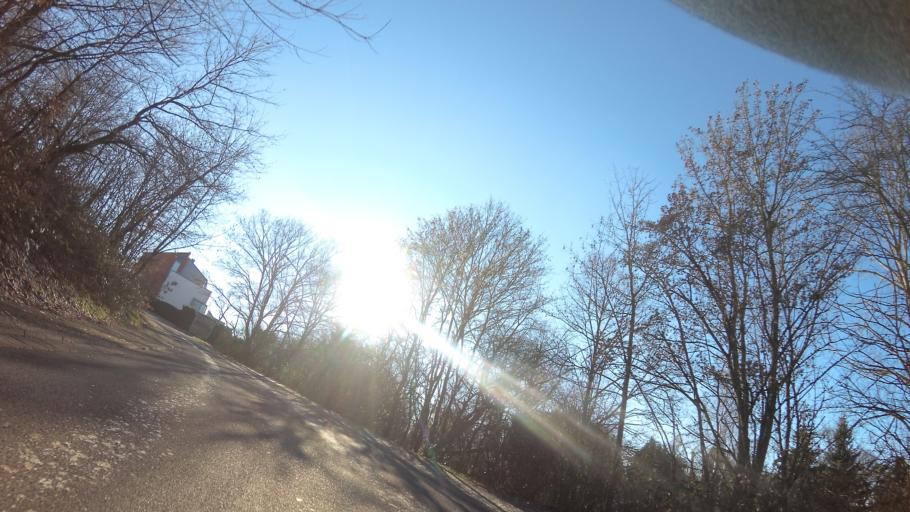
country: DE
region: Saarland
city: Saarlouis
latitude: 49.2989
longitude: 6.7303
